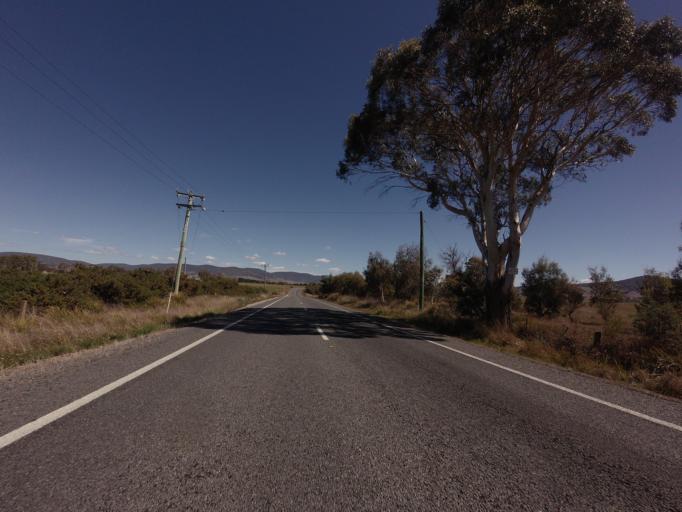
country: AU
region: Tasmania
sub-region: Northern Midlands
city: Evandale
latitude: -41.7743
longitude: 147.7343
